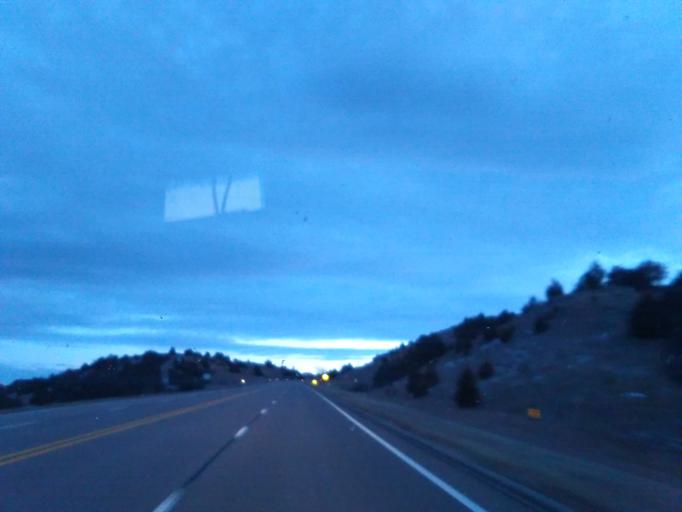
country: US
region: Nebraska
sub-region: Garden County
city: Oshkosh
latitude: 41.2638
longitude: -102.1096
